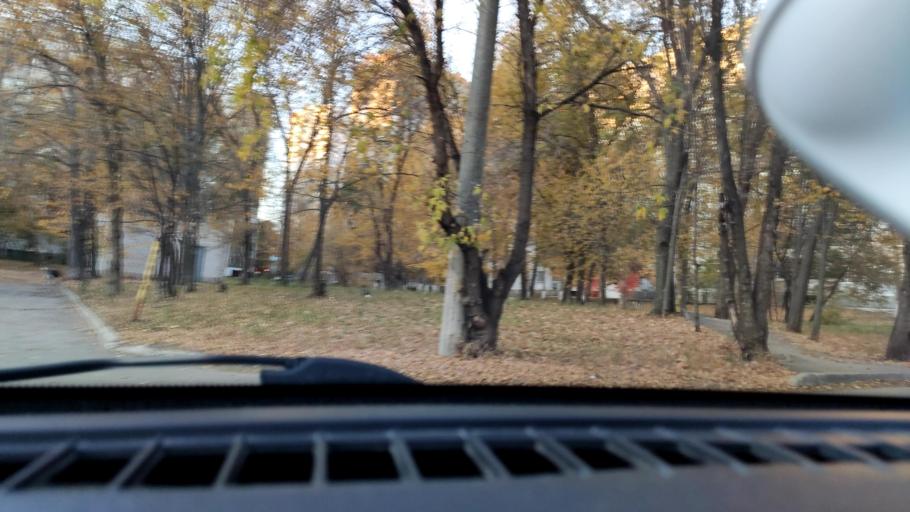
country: RU
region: Samara
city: Samara
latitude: 53.2502
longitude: 50.2311
